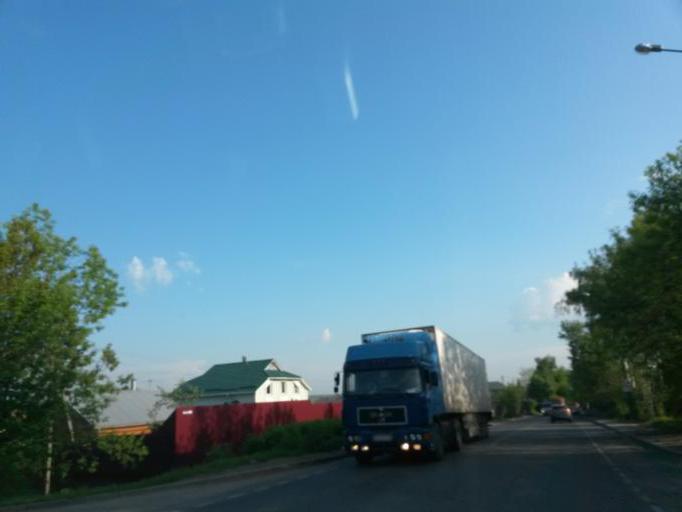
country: RU
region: Moskovskaya
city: Yam
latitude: 55.4633
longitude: 37.7015
